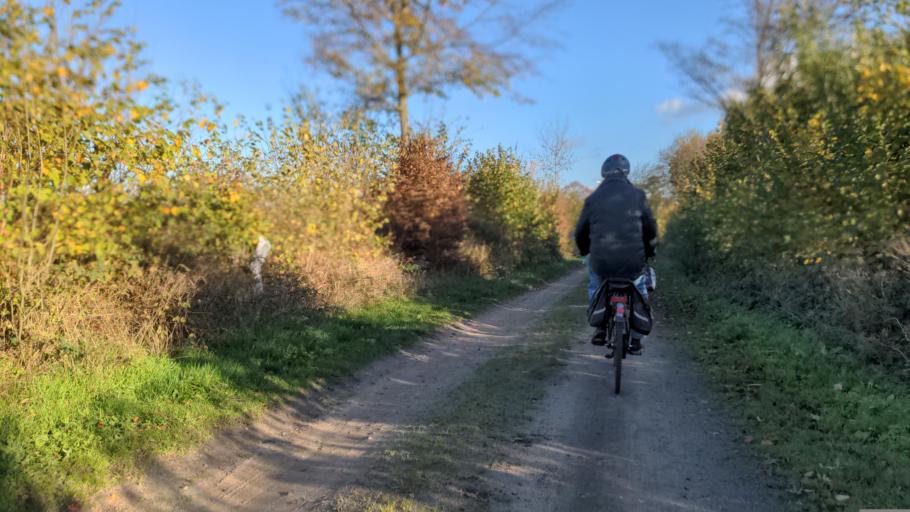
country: DE
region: Schleswig-Holstein
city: Ratekau
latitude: 53.9387
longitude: 10.7751
